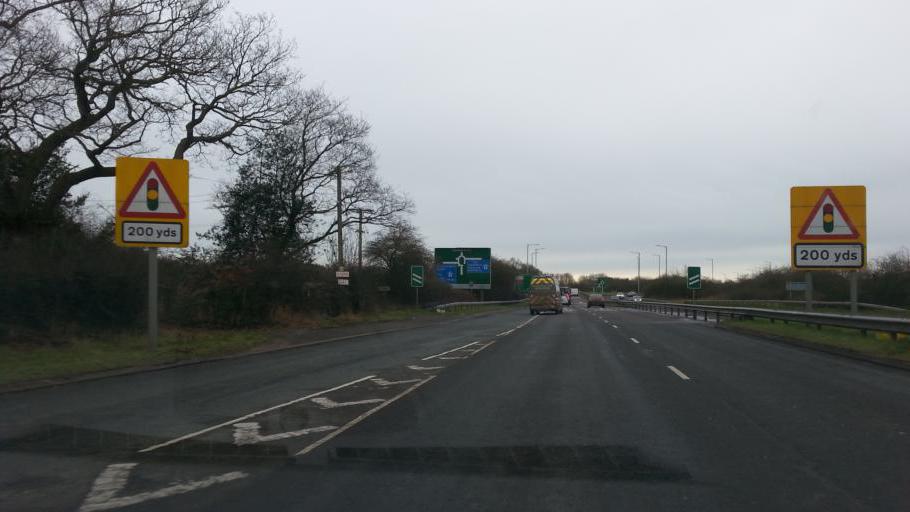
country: GB
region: England
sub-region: Solihull
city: Tidbury Green
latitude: 52.3581
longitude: -1.8880
